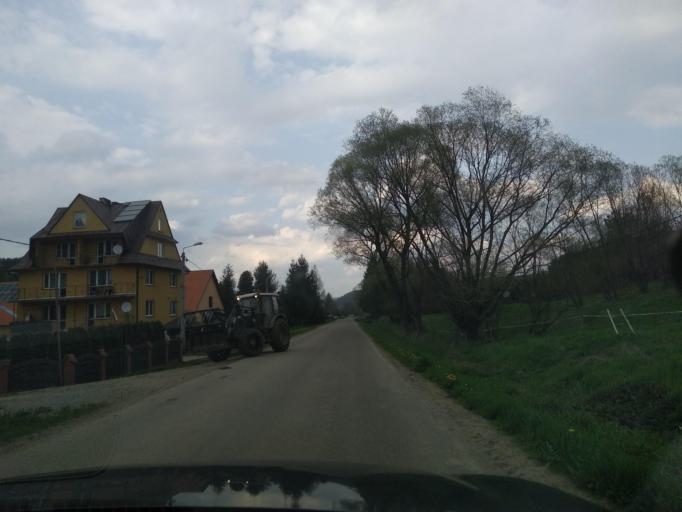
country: PL
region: Subcarpathian Voivodeship
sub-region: Powiat sanocki
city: Czaszyn
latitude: 49.3967
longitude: 22.2160
